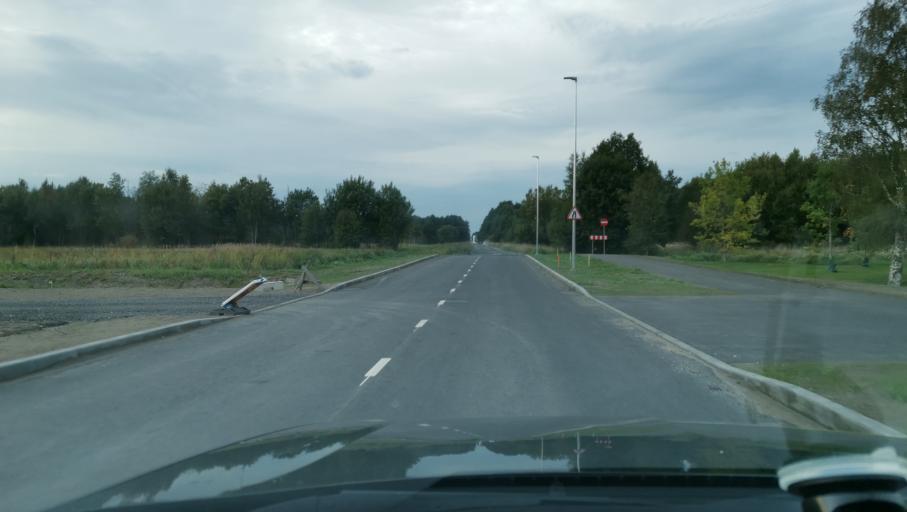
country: EE
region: Harju
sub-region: Saue vald
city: Laagri
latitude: 59.4195
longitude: 24.6299
